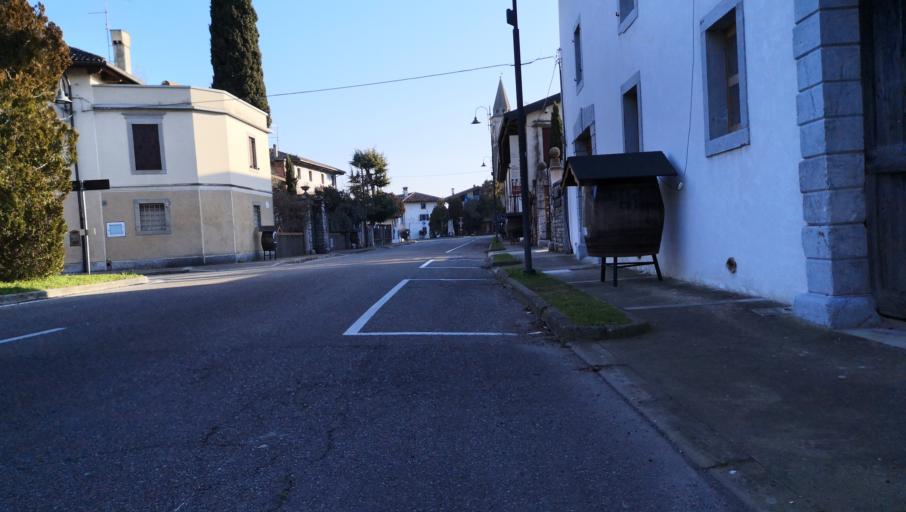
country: IT
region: Friuli Venezia Giulia
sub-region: Provincia di Udine
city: Lauzacco
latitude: 45.9653
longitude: 13.2963
